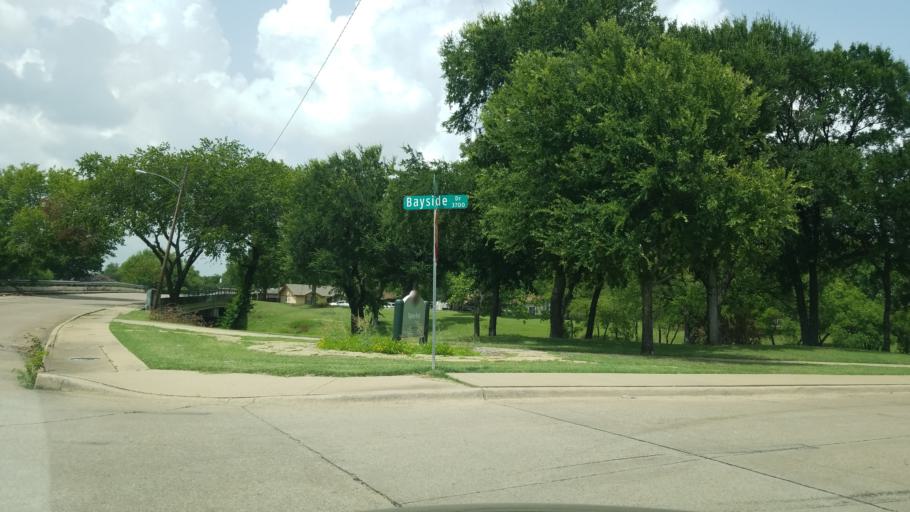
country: US
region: Texas
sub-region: Dallas County
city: Cockrell Hill
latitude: 32.7886
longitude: -96.8825
